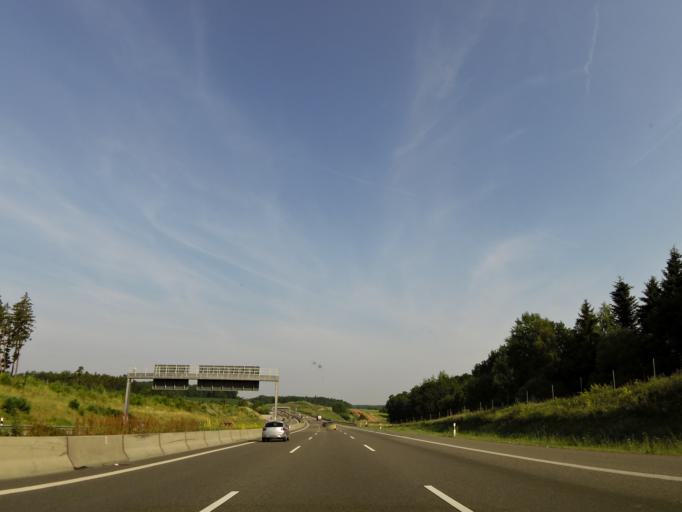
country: DE
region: Baden-Wuerttemberg
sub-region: Regierungsbezirk Stuttgart
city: Rutesheim
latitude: 48.8159
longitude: 8.9134
